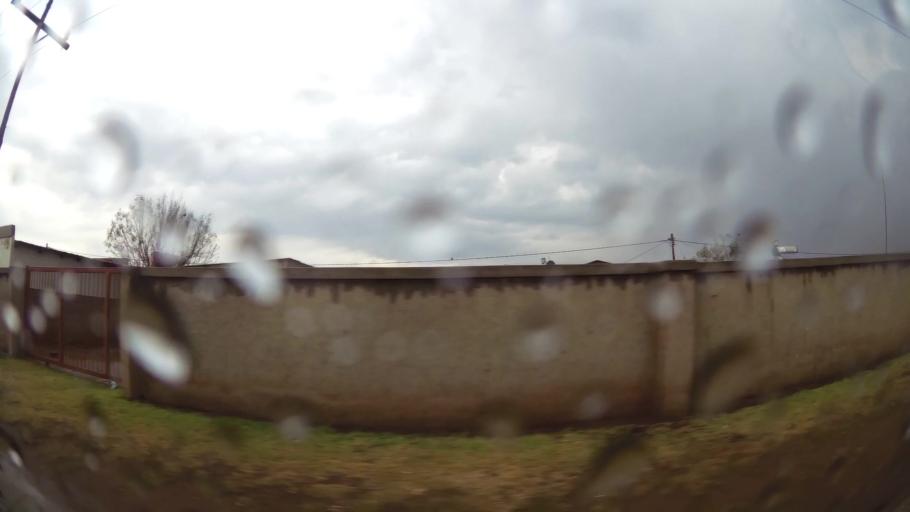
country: ZA
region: Gauteng
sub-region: Ekurhuleni Metropolitan Municipality
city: Germiston
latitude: -26.3753
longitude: 28.1509
